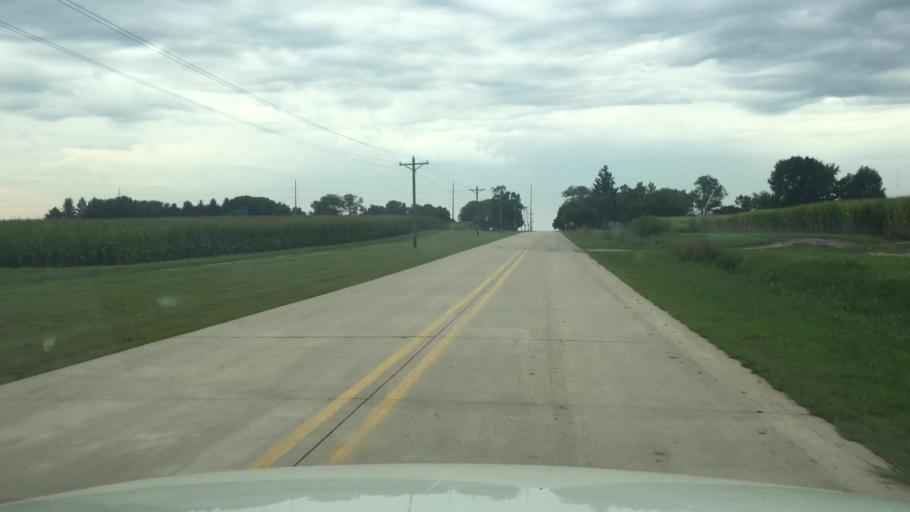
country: US
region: Iowa
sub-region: Story County
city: Huxley
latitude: 41.8819
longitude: -93.5809
